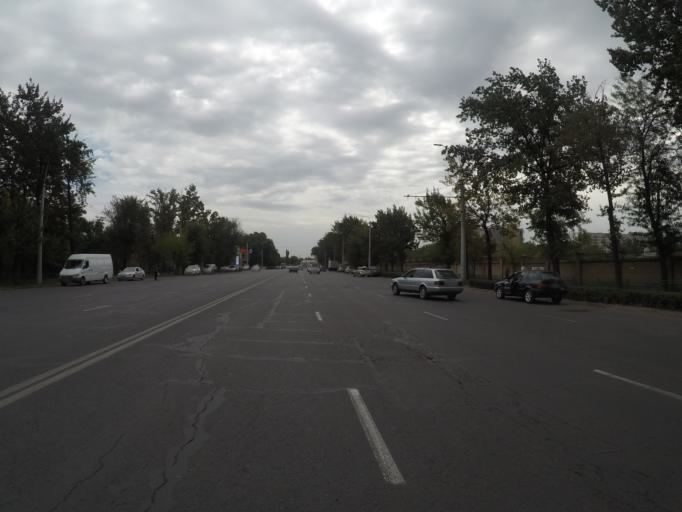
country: KG
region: Chuy
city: Bishkek
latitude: 42.8849
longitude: 74.5709
